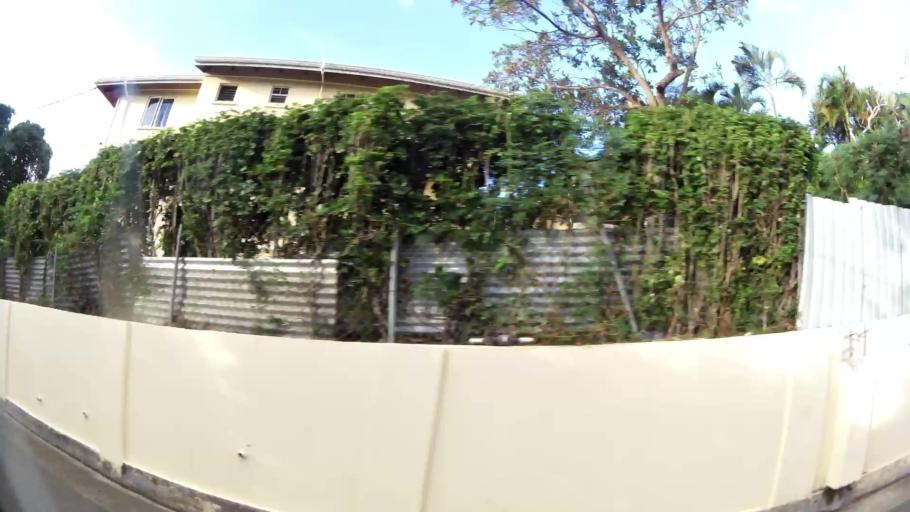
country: LC
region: Gros-Islet
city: Gros Islet
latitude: 14.0819
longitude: -60.9435
